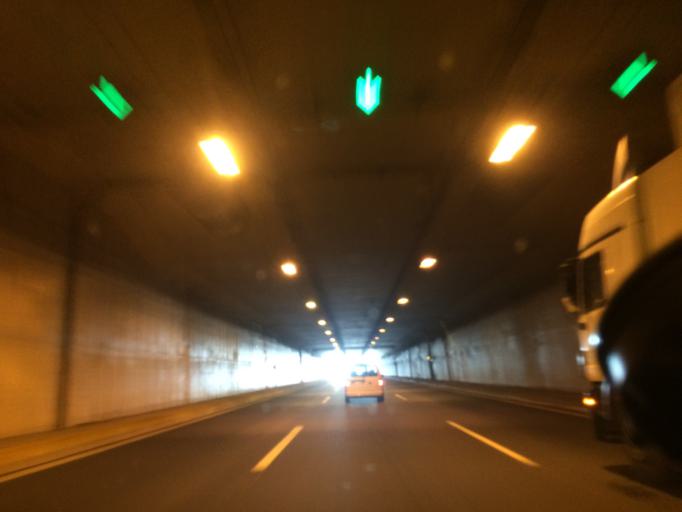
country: GR
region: Central Macedonia
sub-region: Nomos Pierias
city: Katerini
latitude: 40.2754
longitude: 22.5212
